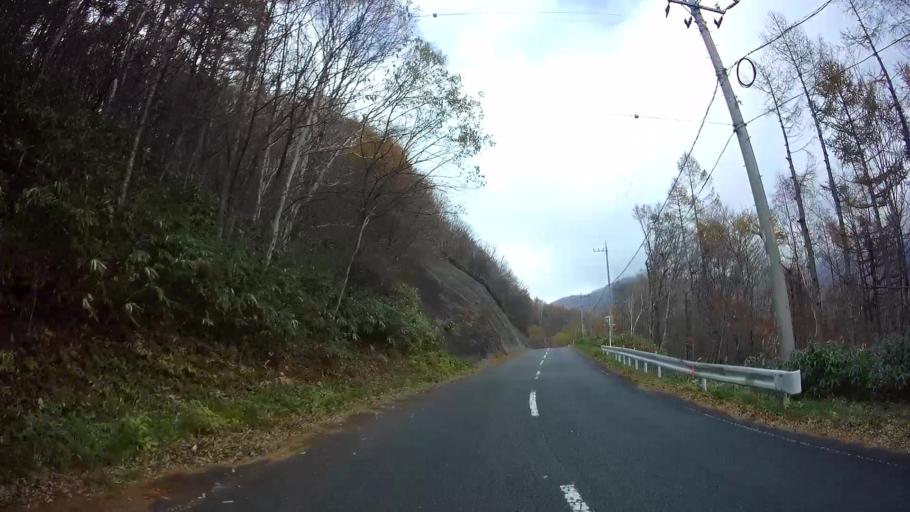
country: JP
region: Gunma
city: Nakanojomachi
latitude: 36.6787
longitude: 138.6639
